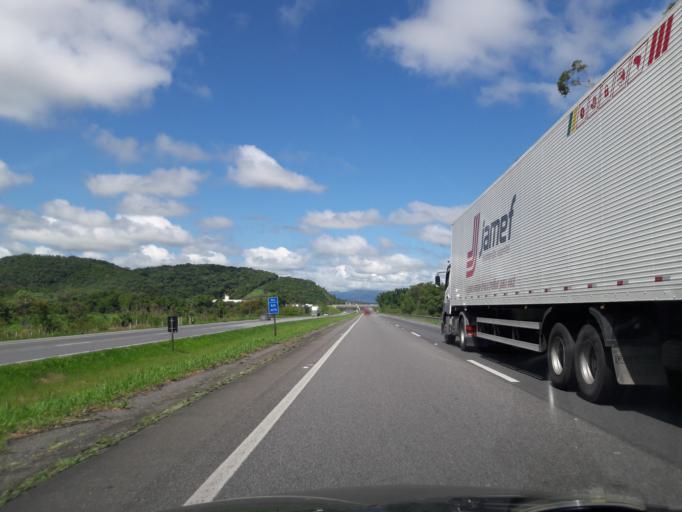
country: BR
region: Sao Paulo
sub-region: Jacupiranga
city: Jacupiranga
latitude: -24.6824
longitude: -47.9851
